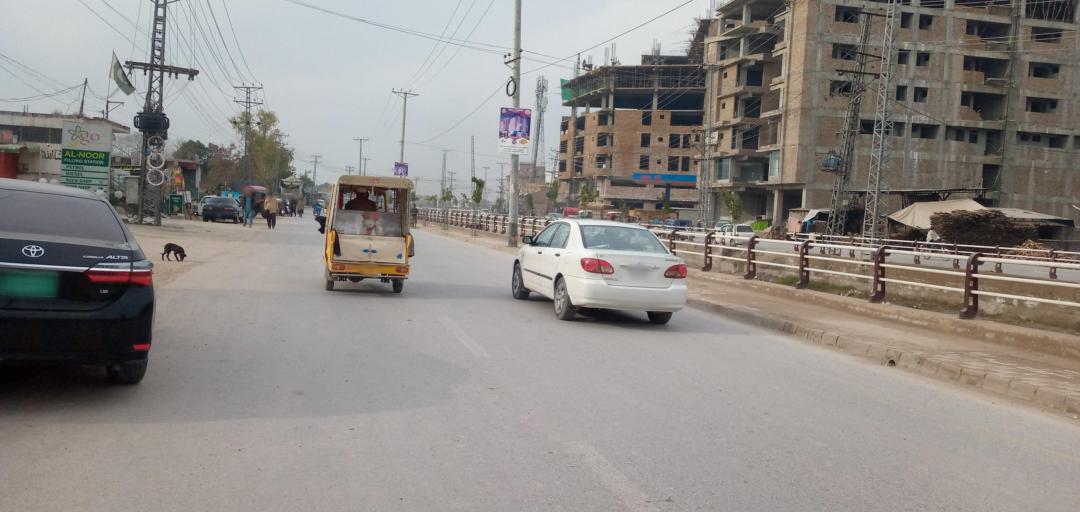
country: PK
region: Khyber Pakhtunkhwa
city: Peshawar
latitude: 34.0048
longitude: 71.4644
